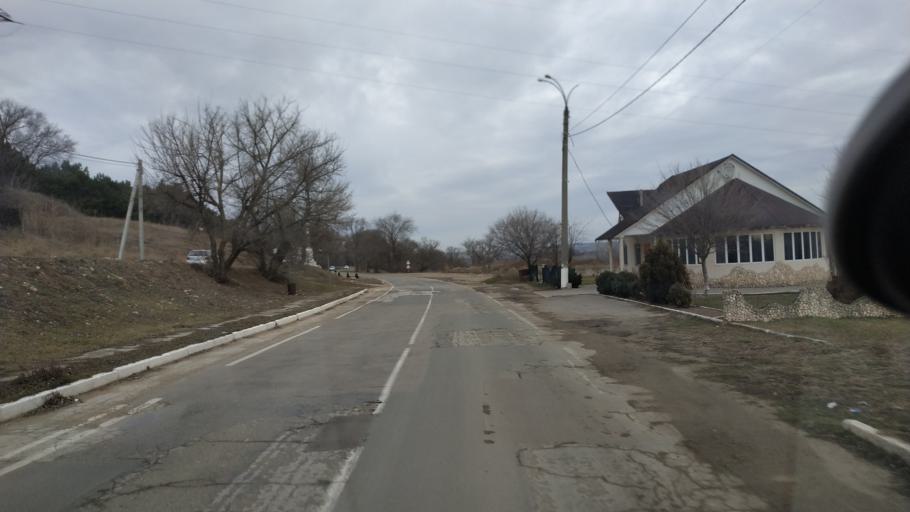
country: MD
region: Criuleni
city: Criuleni
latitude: 47.2239
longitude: 29.1628
